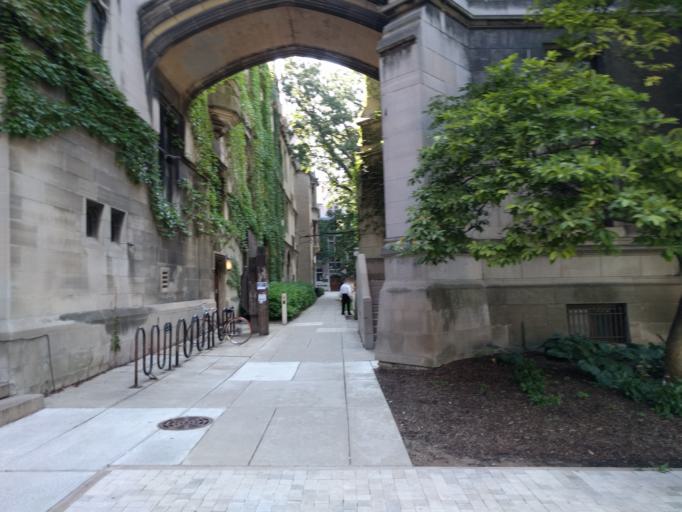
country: US
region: Illinois
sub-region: Cook County
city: Chicago
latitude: 41.7883
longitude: -87.5997
